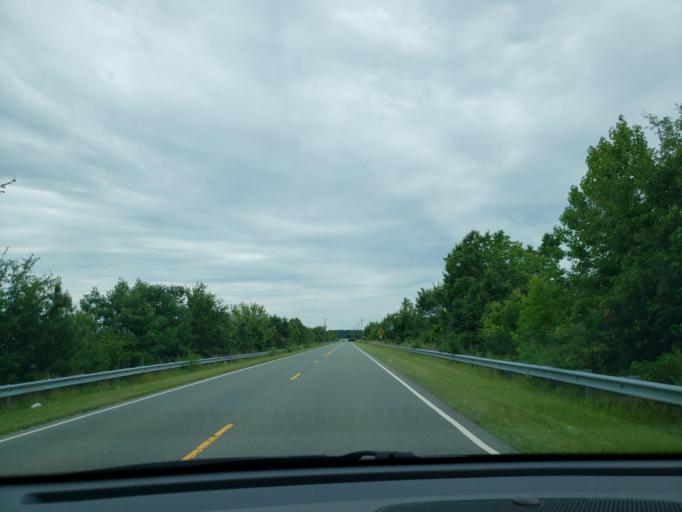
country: US
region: North Carolina
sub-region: Chatham County
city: Fearrington Village
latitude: 35.7871
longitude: -79.0098
